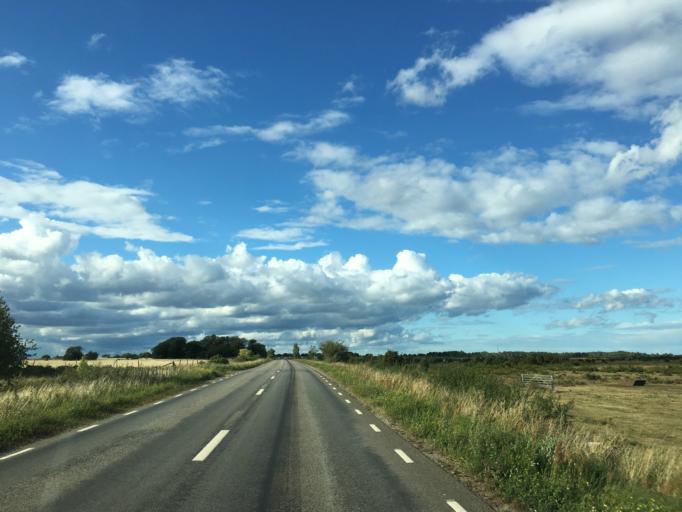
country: SE
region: Kalmar
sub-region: Morbylanga Kommun
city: Moerbylanga
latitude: 56.4915
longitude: 16.4261
